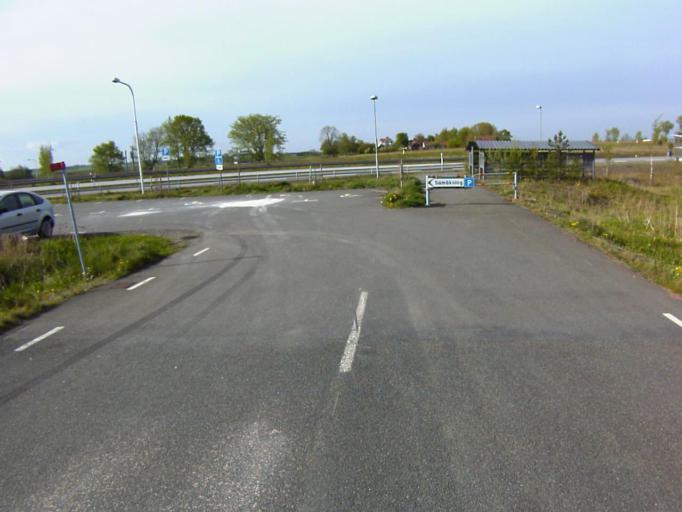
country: SE
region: Skane
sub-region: Kristianstads Kommun
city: Fjalkinge
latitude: 56.0350
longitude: 14.2683
